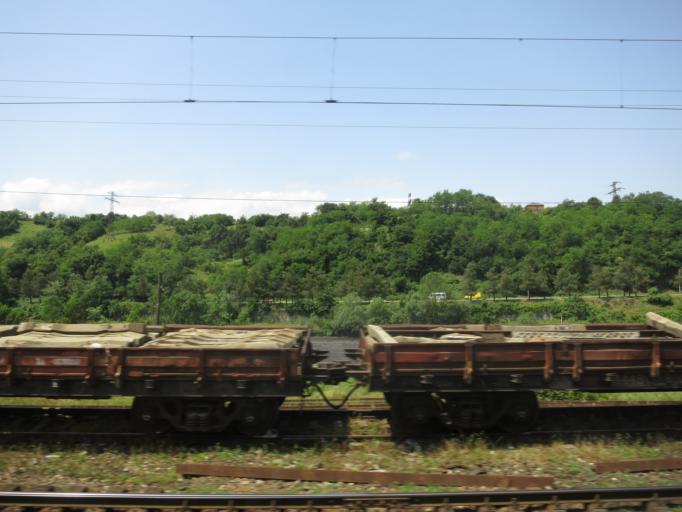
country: GE
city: Shorapani
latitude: 42.0980
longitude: 43.0770
